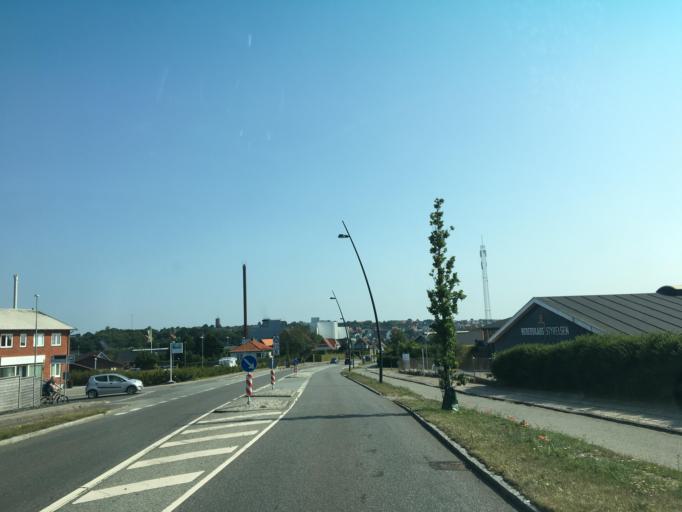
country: DK
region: North Denmark
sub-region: Thisted Kommune
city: Thisted
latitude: 56.9485
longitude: 8.6626
